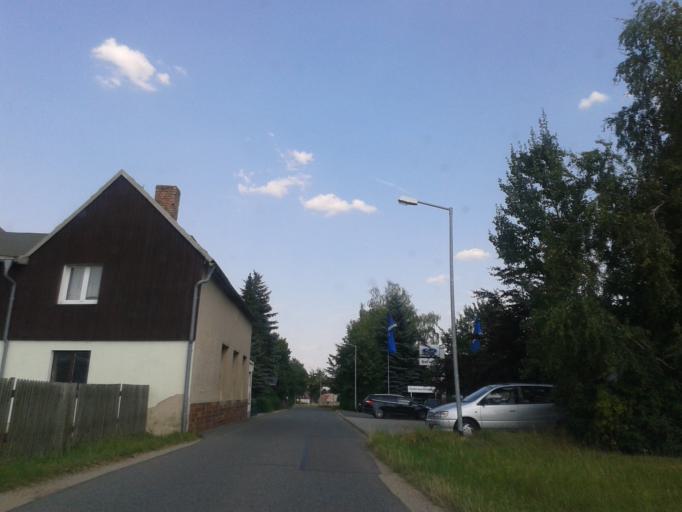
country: DE
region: Saxony
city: Niederschona
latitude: 50.9822
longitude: 13.4294
